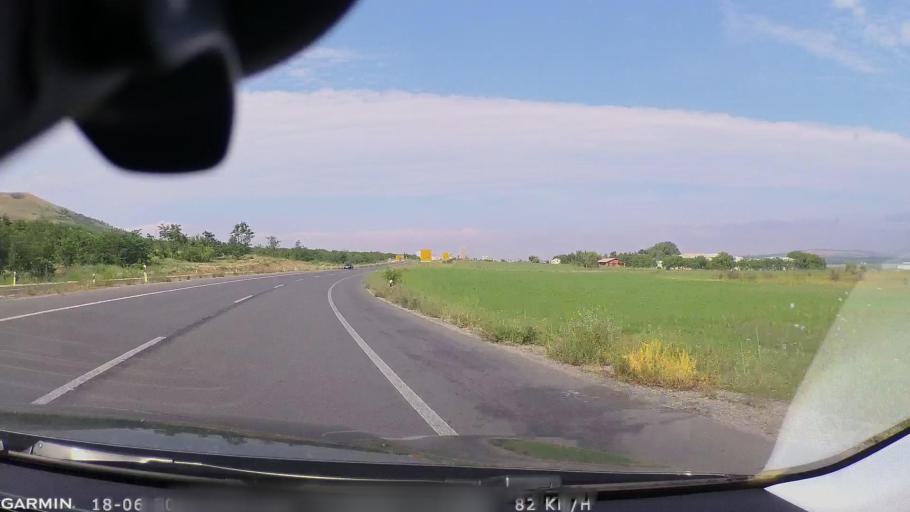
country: MK
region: Sveti Nikole
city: Sveti Nikole
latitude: 41.8270
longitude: 22.0056
